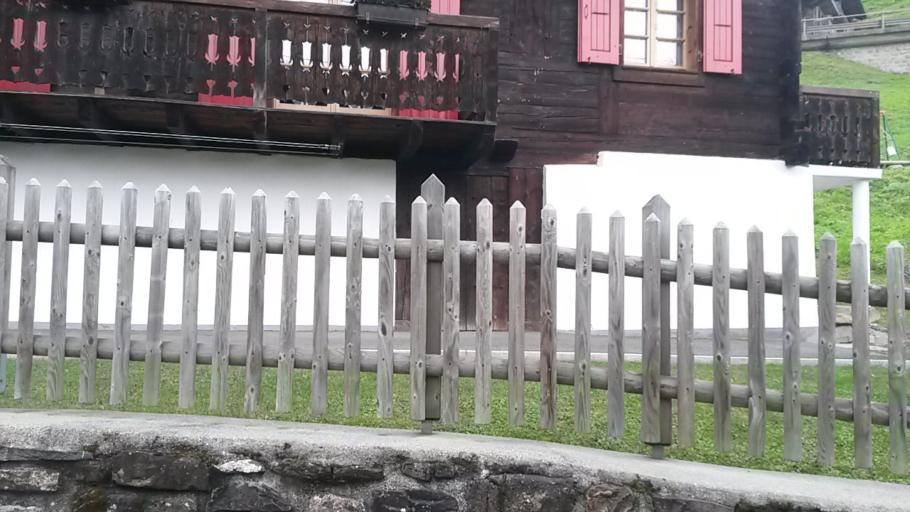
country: CH
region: Valais
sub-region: Monthey District
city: Champery
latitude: 46.1970
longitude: 6.8870
